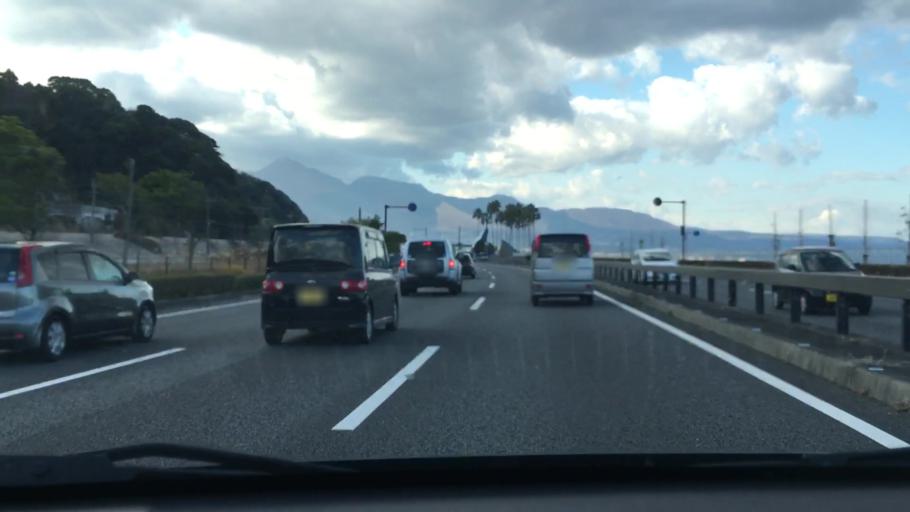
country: JP
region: Oita
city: Oita
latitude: 33.2544
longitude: 131.5623
